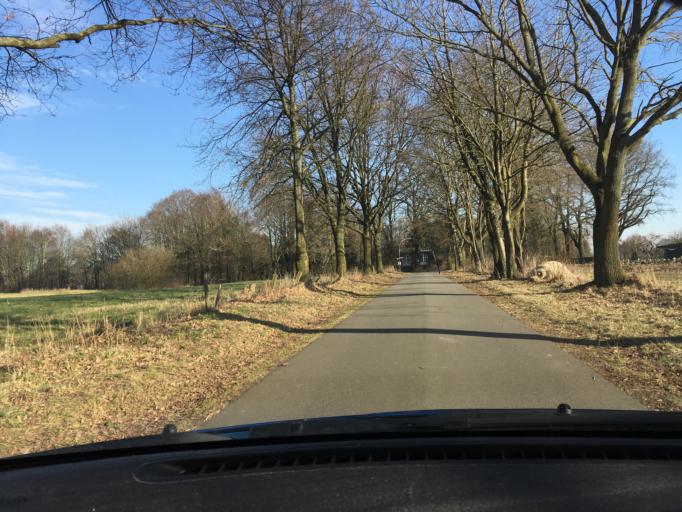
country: DE
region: Lower Saxony
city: Seevetal
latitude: 53.4006
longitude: 9.9846
